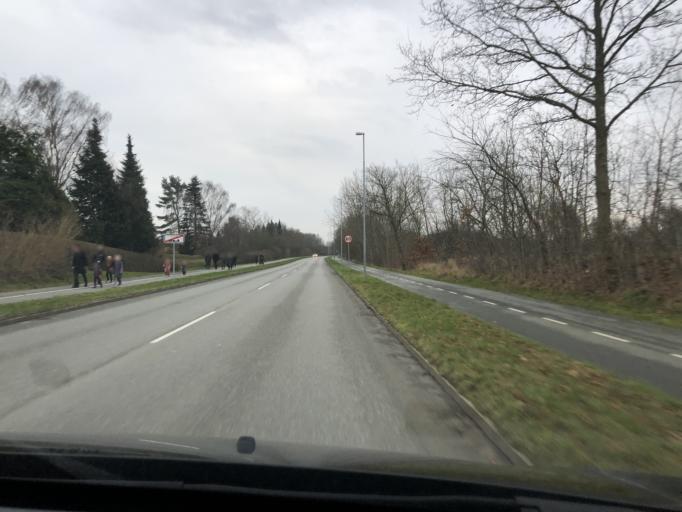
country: DK
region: South Denmark
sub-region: Svendborg Kommune
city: Svendborg
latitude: 55.0864
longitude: 10.6169
